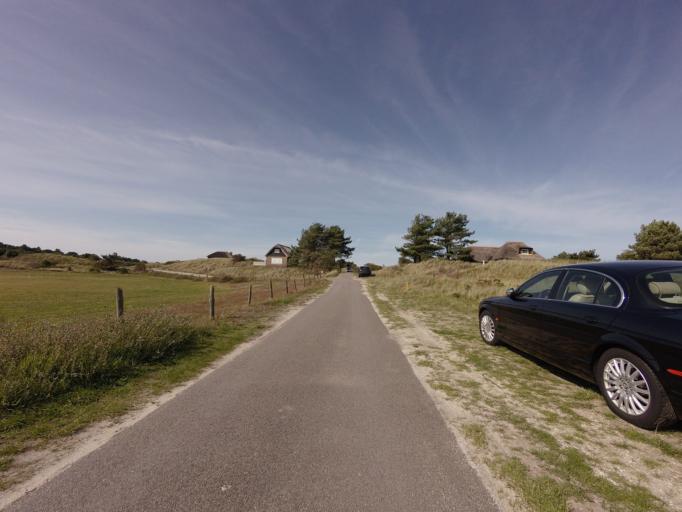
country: NL
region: Friesland
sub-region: Gemeente Ameland
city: Nes
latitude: 53.4537
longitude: 5.7726
